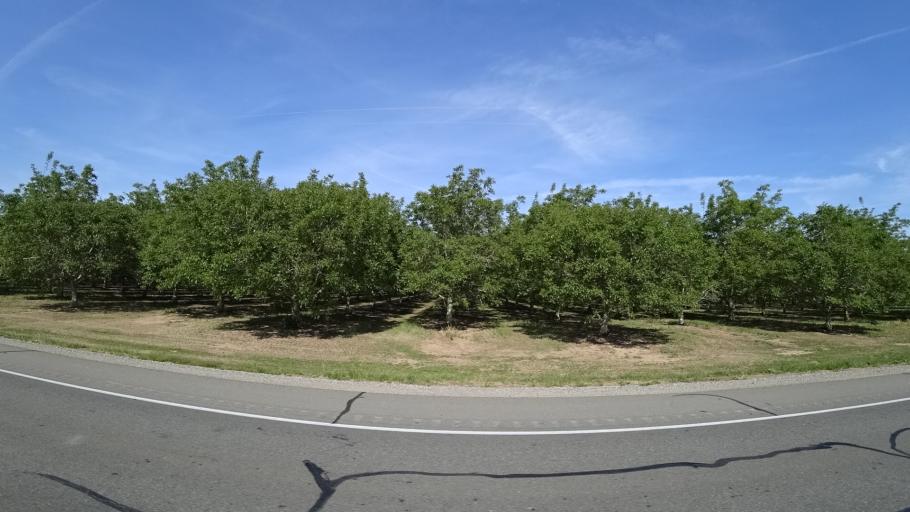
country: US
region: California
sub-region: Tehama County
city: Los Molinos
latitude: 39.9938
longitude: -122.0861
